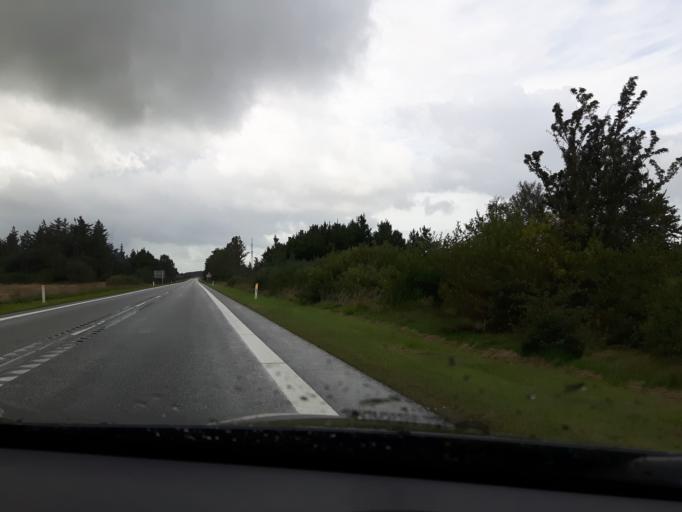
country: DK
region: North Denmark
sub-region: Jammerbugt Kommune
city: Fjerritslev
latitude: 57.0596
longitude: 9.1863
